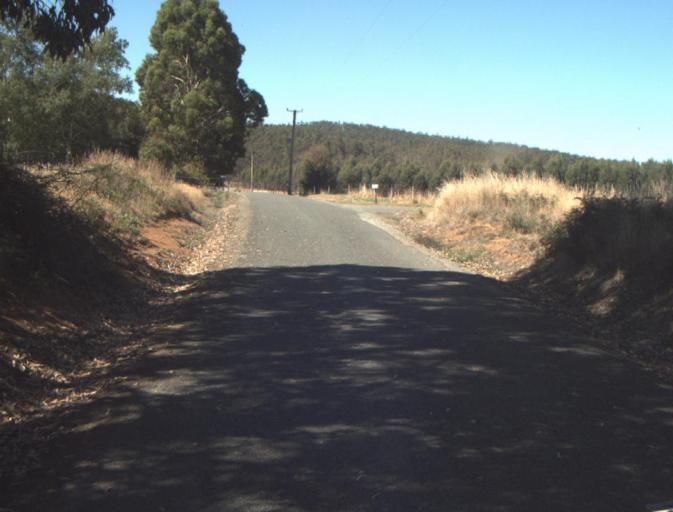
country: AU
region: Tasmania
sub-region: Launceston
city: Newstead
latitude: -41.3190
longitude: 147.3197
